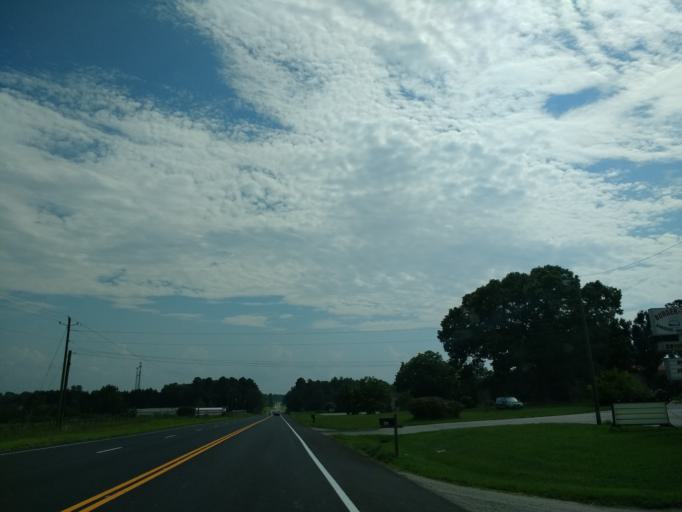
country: US
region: Georgia
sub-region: White County
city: Cleveland
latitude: 34.4833
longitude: -83.7631
